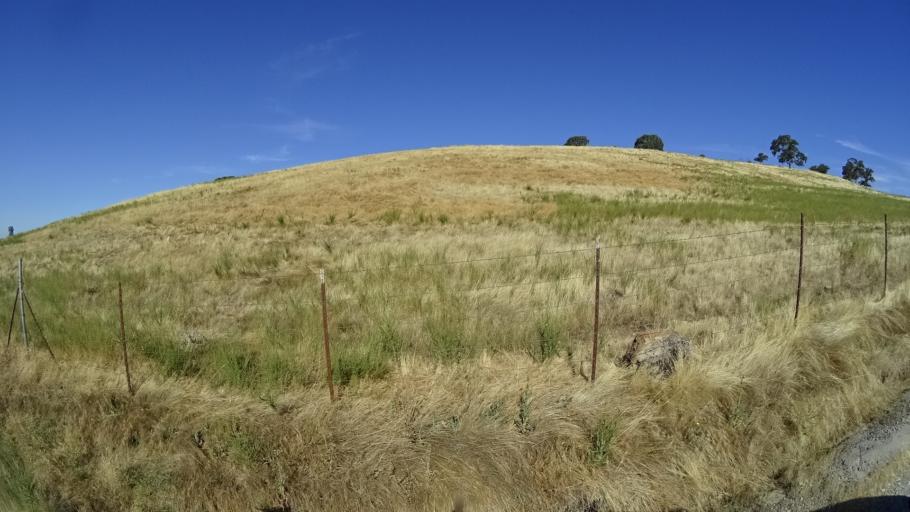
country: US
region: California
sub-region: Calaveras County
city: Valley Springs
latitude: 38.2298
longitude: -120.7949
